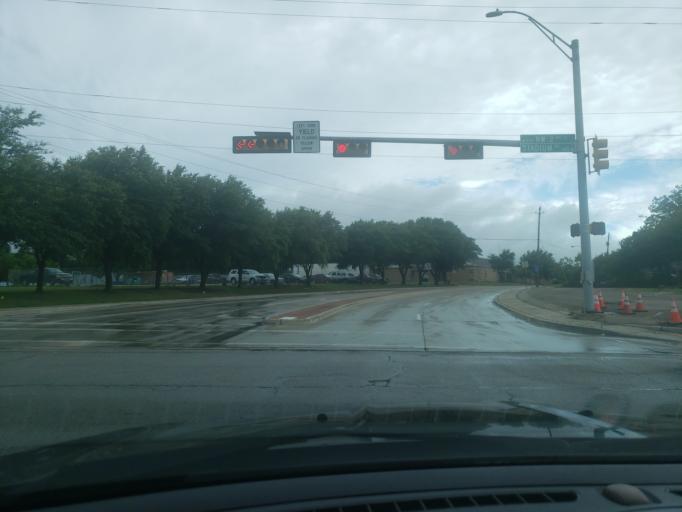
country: US
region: Texas
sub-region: Dallas County
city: Grand Prairie
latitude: 32.7492
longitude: -97.0055
